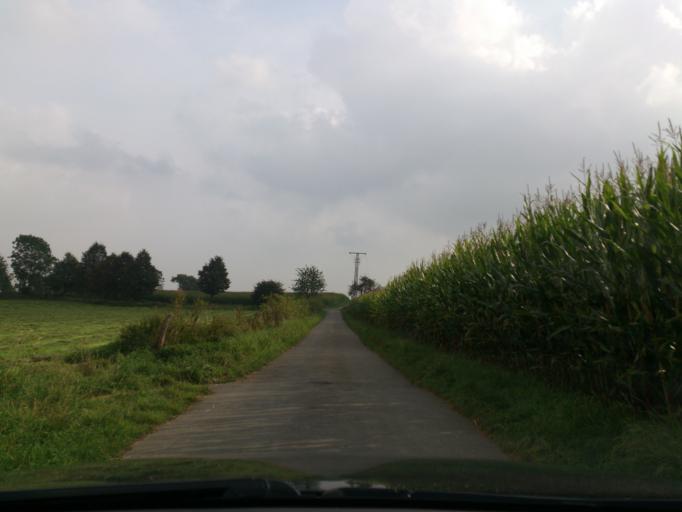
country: DE
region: North Rhine-Westphalia
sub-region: Regierungsbezirk Detmold
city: Willebadessen
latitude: 51.5766
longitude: 9.0354
